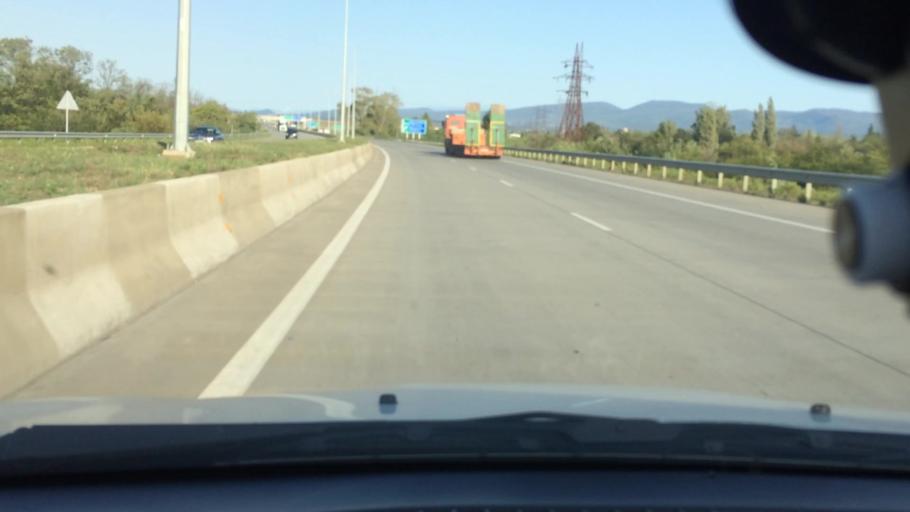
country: GE
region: Imereti
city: Zestap'oni
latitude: 42.1535
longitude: 42.9582
